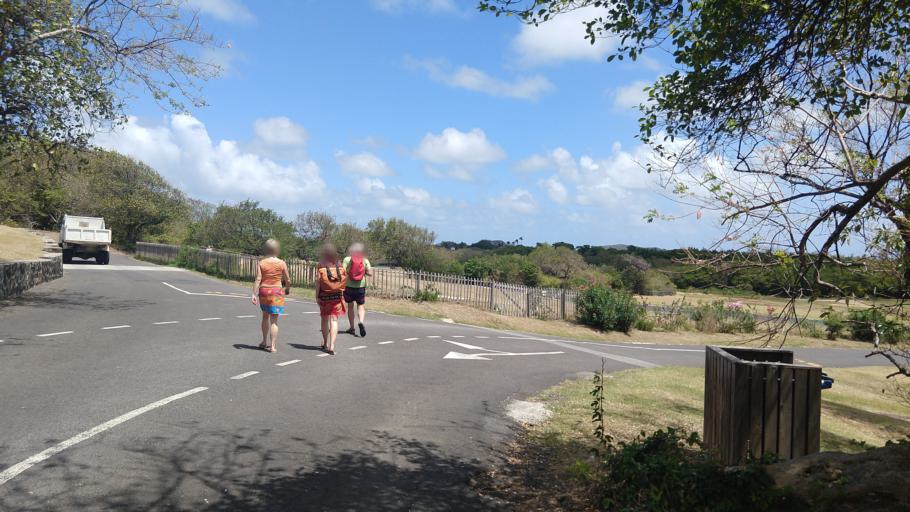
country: VC
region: Grenadines
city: Port Elizabeth
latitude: 12.8858
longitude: -61.1847
